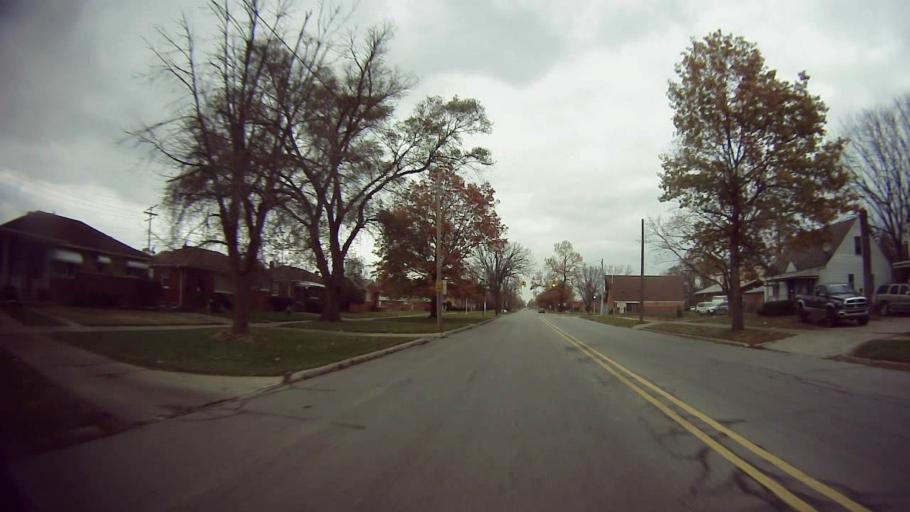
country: US
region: Michigan
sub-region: Macomb County
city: Warren
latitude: 42.4265
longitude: -83.0043
